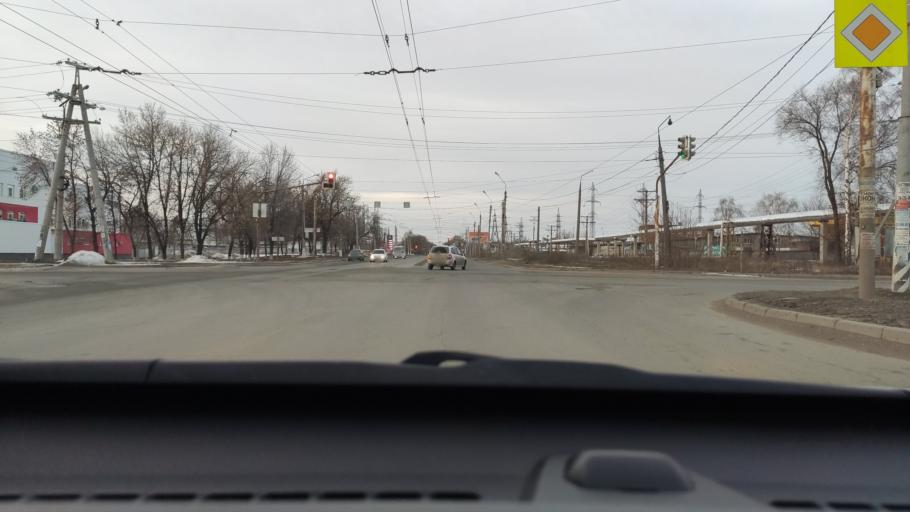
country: RU
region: Samara
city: Tol'yatti
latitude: 53.5347
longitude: 49.4362
